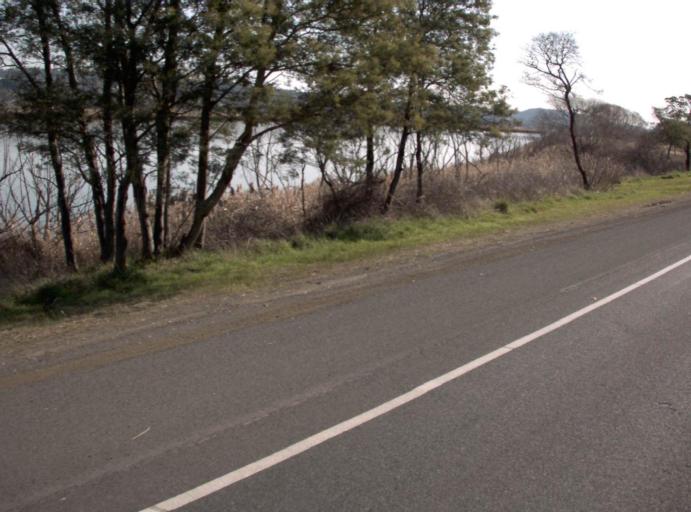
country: AU
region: Tasmania
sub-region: Launceston
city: Newnham
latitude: -41.4066
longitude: 147.1236
